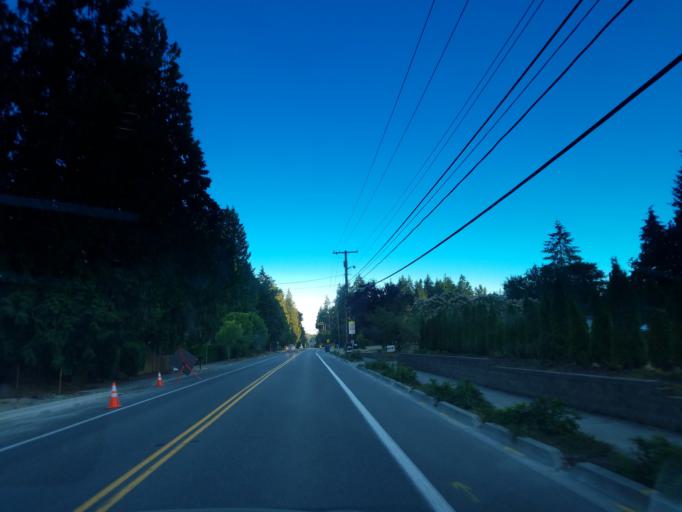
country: US
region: Washington
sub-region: King County
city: City of Sammamish
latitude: 47.6214
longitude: -122.0139
